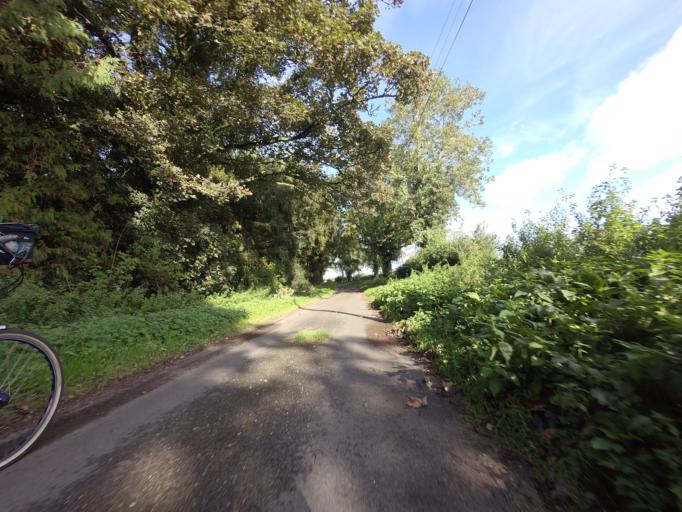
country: GB
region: England
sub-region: Norfolk
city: Fakenham
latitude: 52.8897
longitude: 0.6835
